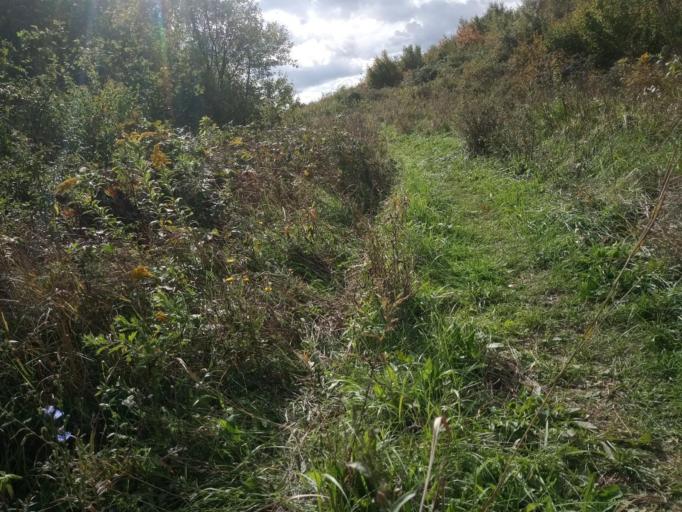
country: HU
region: Pest
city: Csobanka
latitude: 47.6667
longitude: 18.9572
